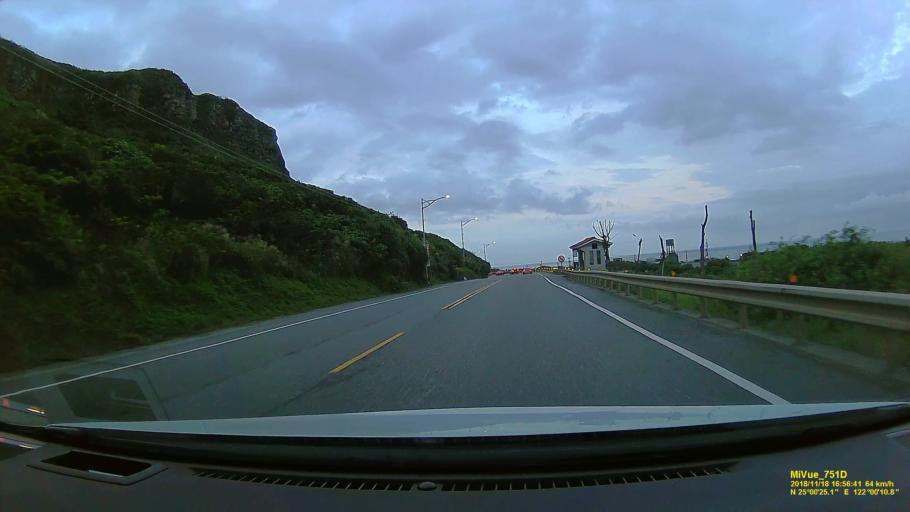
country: TW
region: Taiwan
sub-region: Keelung
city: Keelung
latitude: 25.0065
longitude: 122.0029
